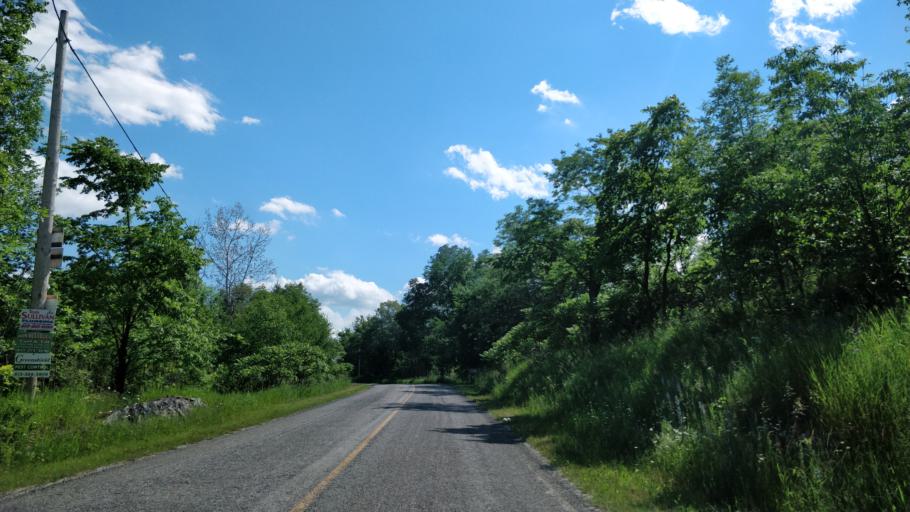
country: CA
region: Ontario
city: Perth
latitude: 44.7375
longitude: -76.5019
